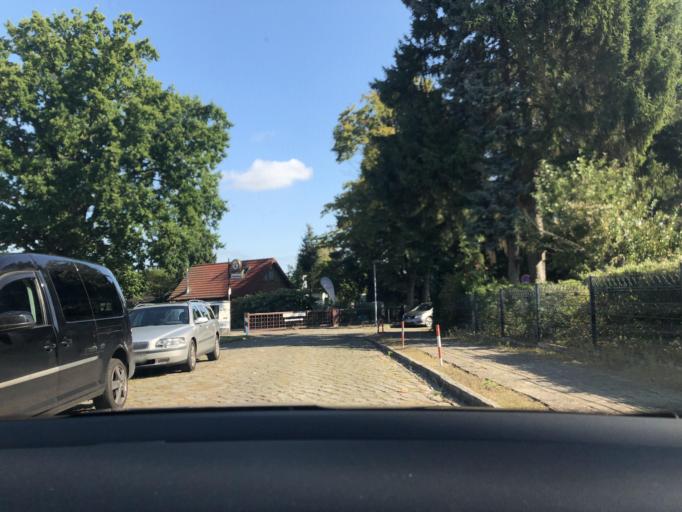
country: DE
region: Brandenburg
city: Erkner
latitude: 52.4220
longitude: 13.7454
